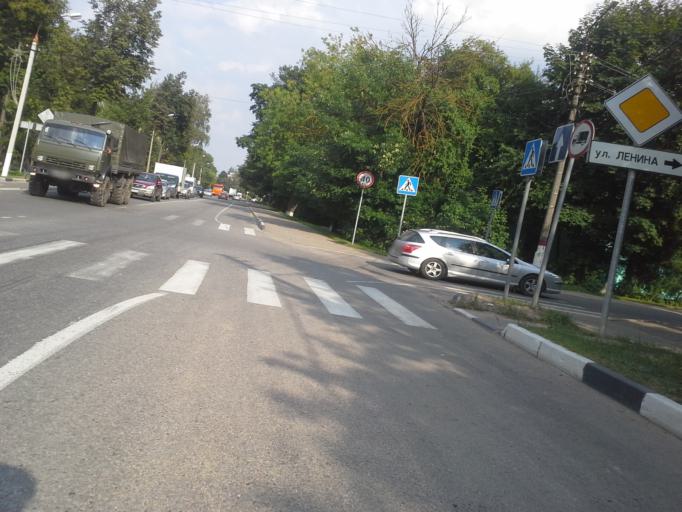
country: RU
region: Moskovskaya
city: Istra
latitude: 55.9201
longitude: 36.8604
